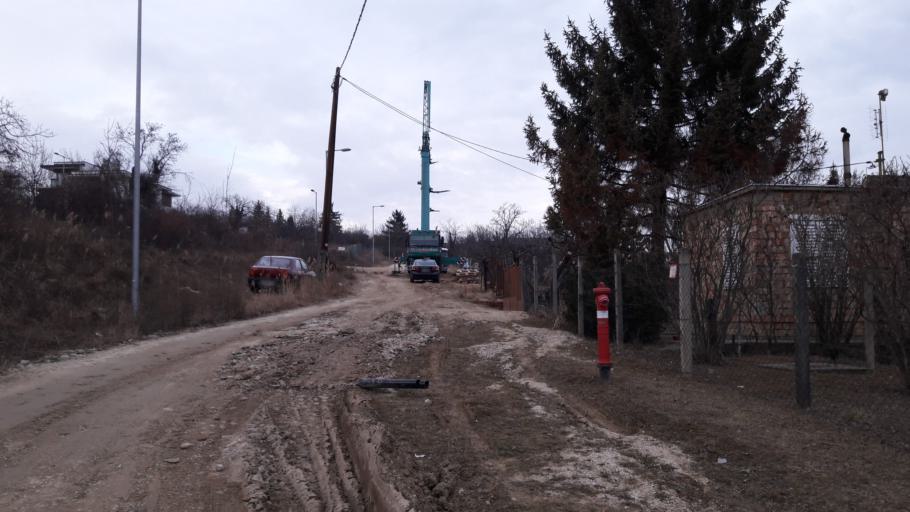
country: HU
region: Pest
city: Budaors
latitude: 47.4651
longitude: 18.9909
